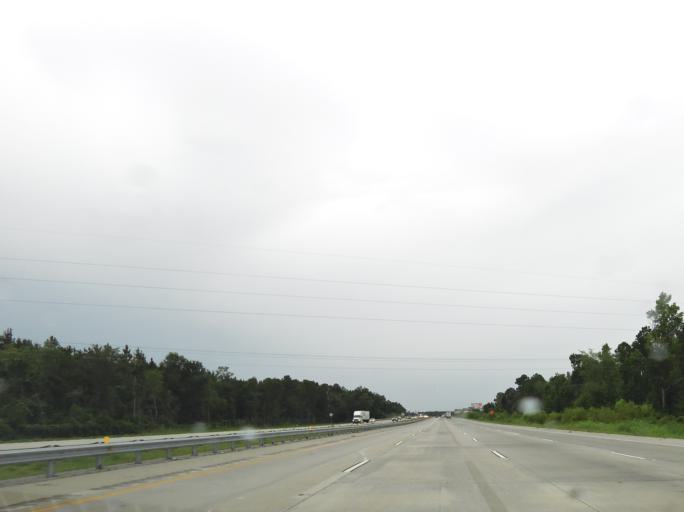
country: US
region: Georgia
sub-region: Dooly County
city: Vienna
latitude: 32.1205
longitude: -83.7617
